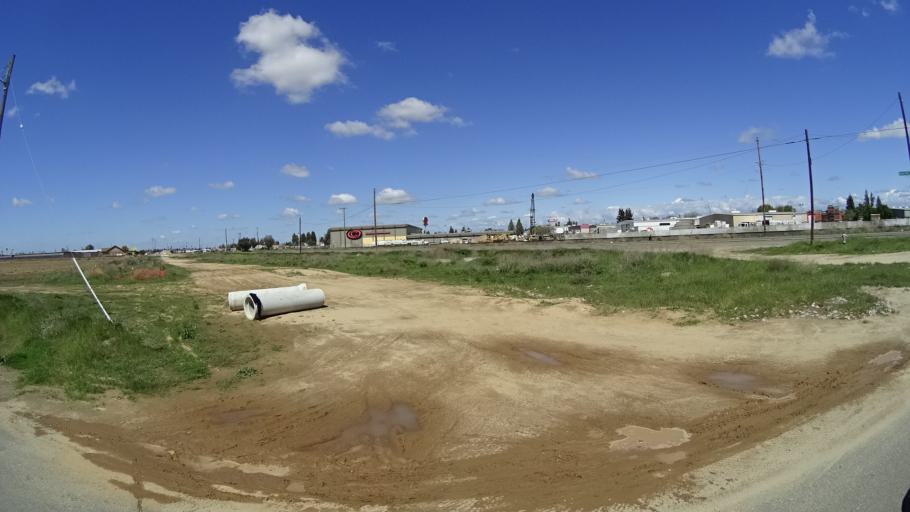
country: US
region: California
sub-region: Fresno County
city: West Park
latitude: 36.8045
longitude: -119.8744
